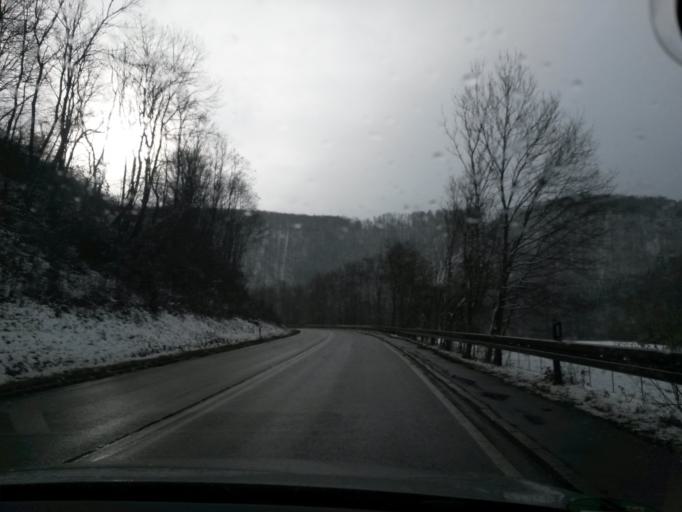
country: DE
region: Baden-Wuerttemberg
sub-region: Regierungsbezirk Stuttgart
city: Geislingen an der Steige
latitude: 48.6013
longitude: 9.8420
